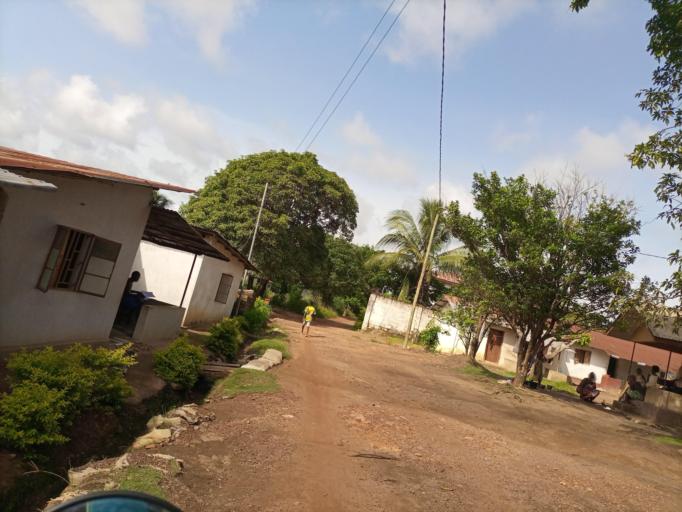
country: SL
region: Southern Province
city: Bo
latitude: 7.9648
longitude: -11.7634
